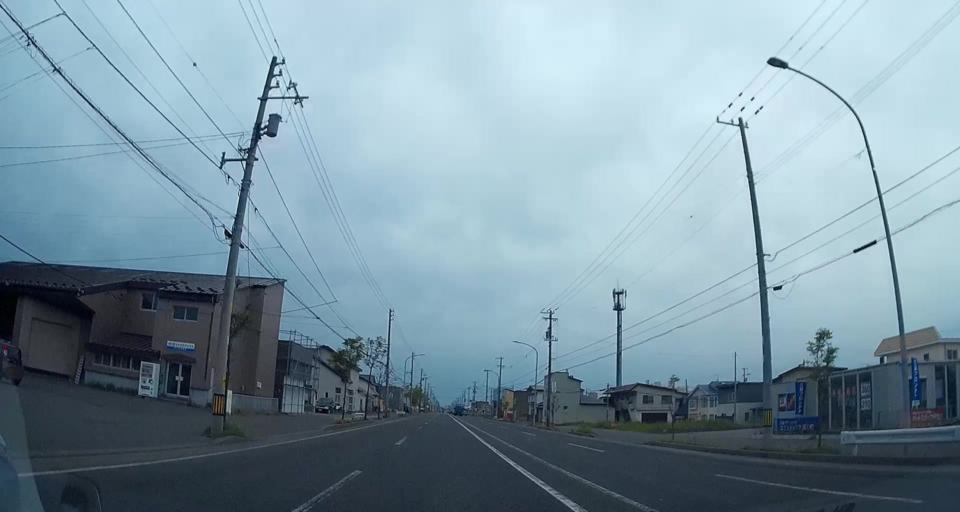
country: JP
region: Hokkaido
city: Tomakomai
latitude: 42.6257
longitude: 141.5873
